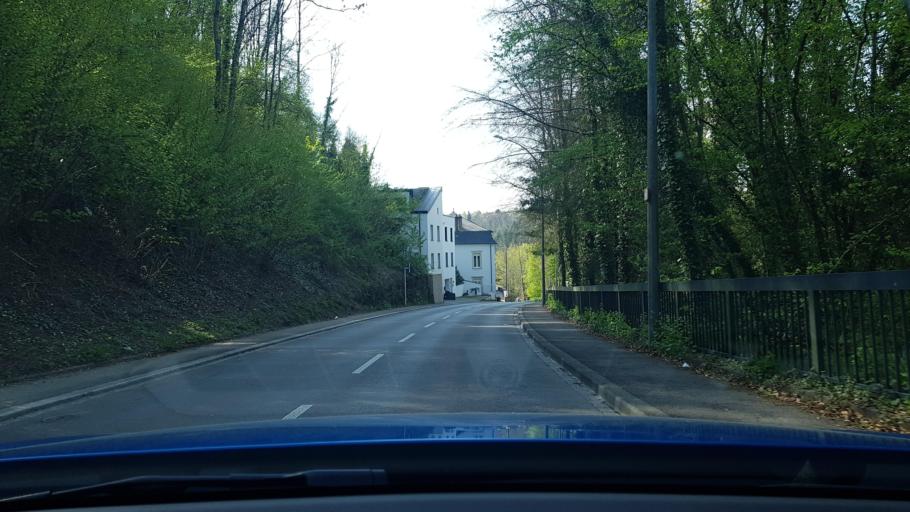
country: LU
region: Luxembourg
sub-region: Canton de Luxembourg
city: Luxembourg
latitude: 49.6273
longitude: 6.1197
